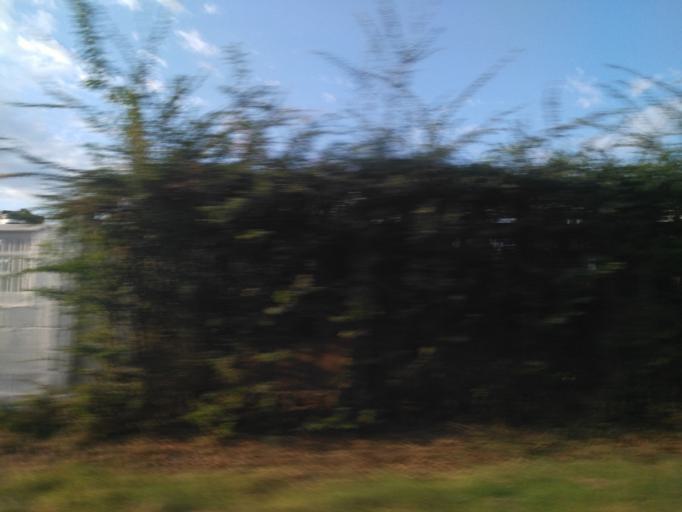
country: TZ
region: Dar es Salaam
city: Magomeni
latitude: -6.7835
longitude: 39.2732
